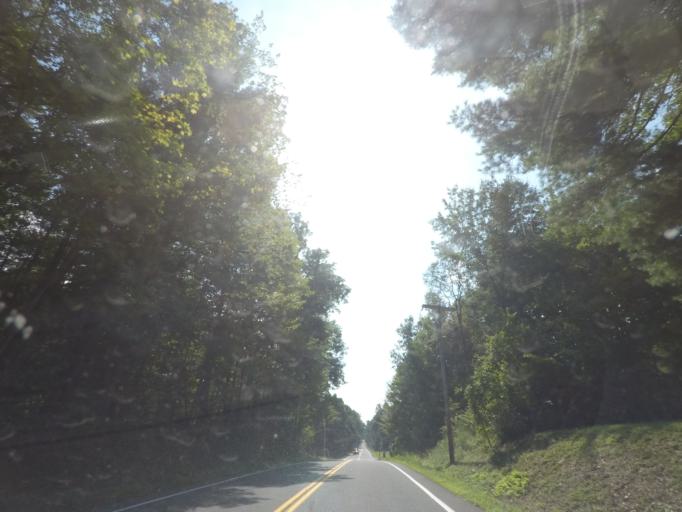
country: US
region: New York
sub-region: Rensselaer County
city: Poestenkill
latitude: 42.8068
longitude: -73.5181
